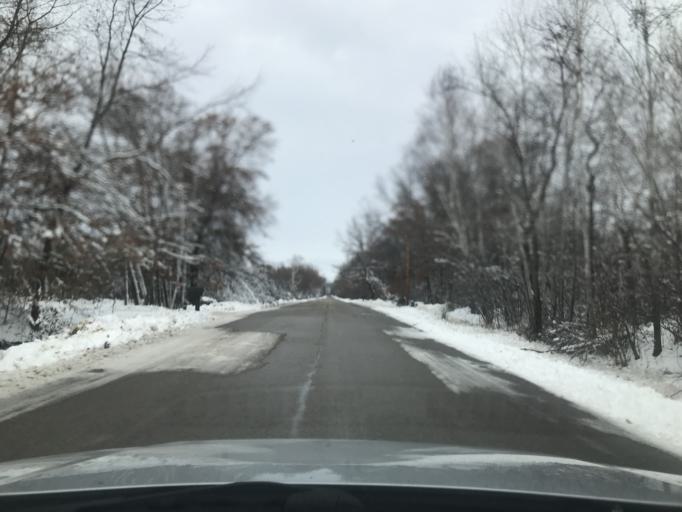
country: US
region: Wisconsin
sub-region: Marinette County
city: Peshtigo
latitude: 45.0764
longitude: -87.7216
